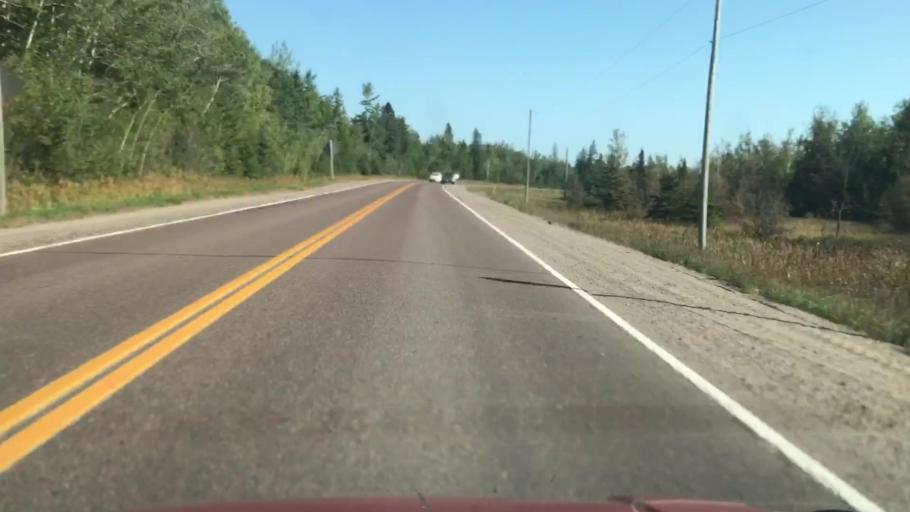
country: CA
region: Ontario
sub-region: Algoma
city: Sault Ste. Marie
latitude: 46.3358
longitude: -84.0077
